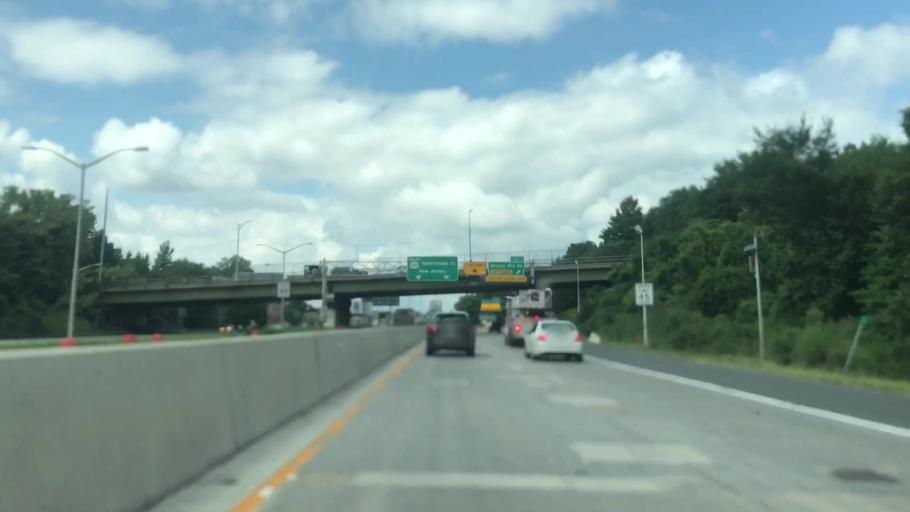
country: US
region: New Jersey
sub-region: Middlesex County
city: Sewaren
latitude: 40.5259
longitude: -74.2289
